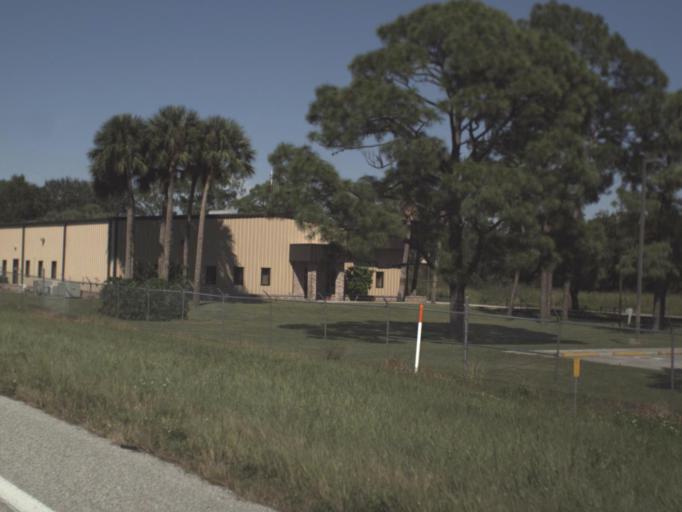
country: US
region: Florida
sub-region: Highlands County
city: Lake Placid
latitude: 27.3522
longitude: -81.3880
